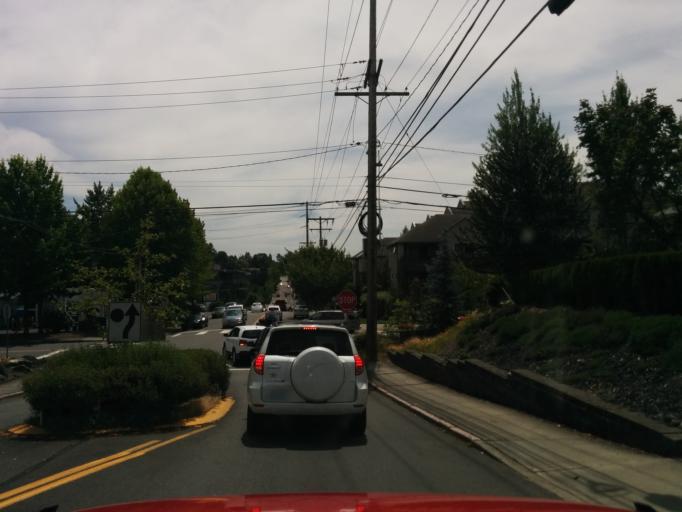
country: US
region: Washington
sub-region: King County
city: Kirkland
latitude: 47.6809
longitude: -122.1971
